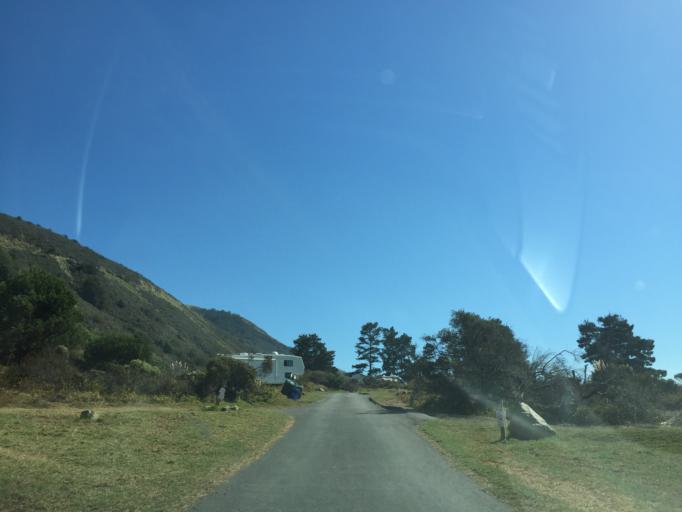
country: US
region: California
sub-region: Monterey County
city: Greenfield
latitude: 35.9908
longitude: -121.4960
